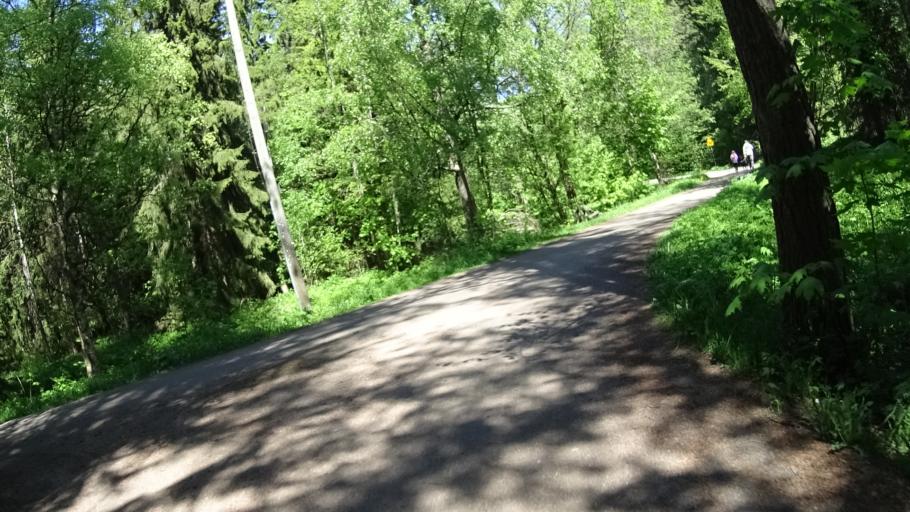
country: FI
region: Uusimaa
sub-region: Helsinki
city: Helsinki
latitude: 60.2281
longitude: 24.9141
